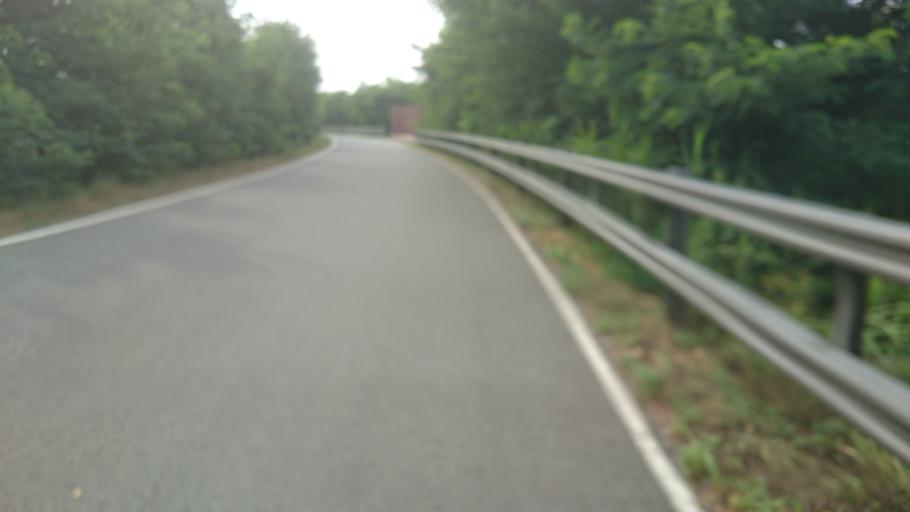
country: KR
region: Gyeongsangbuk-do
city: Gyeongsan-si
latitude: 35.8713
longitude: 128.6749
